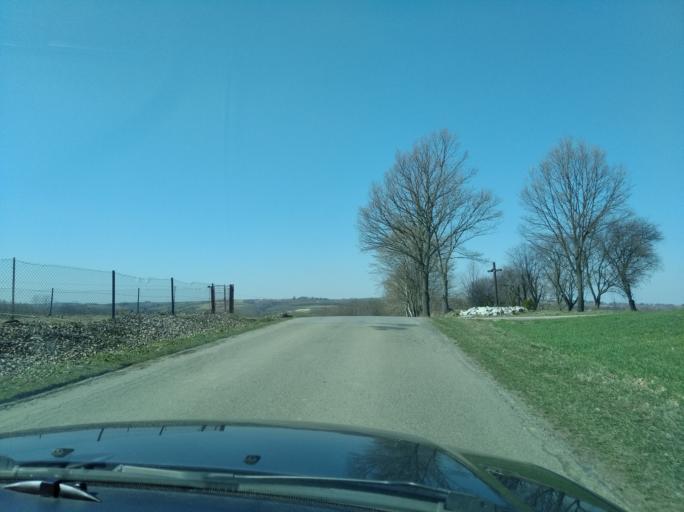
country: PL
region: Subcarpathian Voivodeship
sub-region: Powiat przeworski
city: Pantalowice
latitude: 49.9256
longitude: 22.4526
